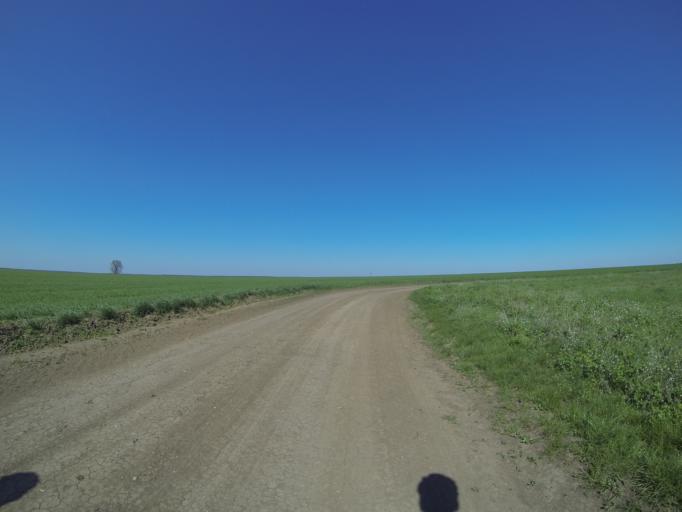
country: RO
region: Dolj
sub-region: Comuna Caloparu
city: Salcuta
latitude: 44.1622
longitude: 23.6640
